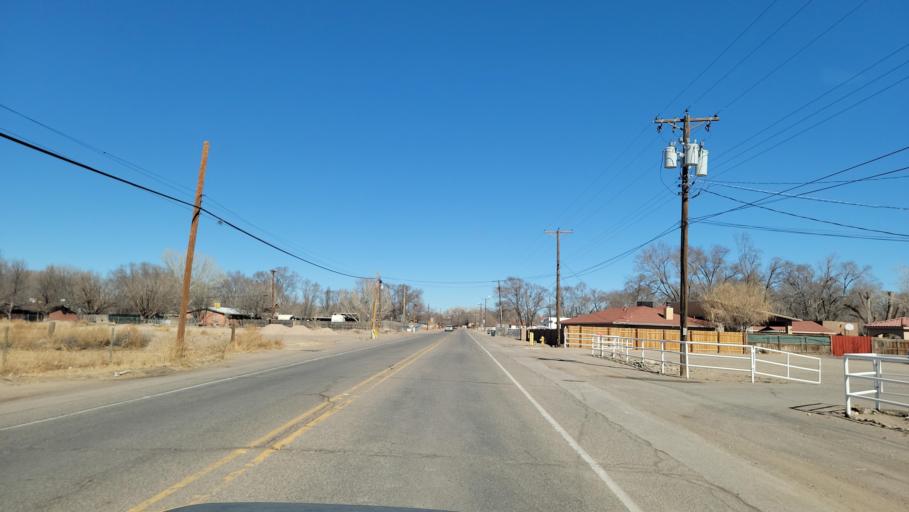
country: US
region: New Mexico
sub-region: Bernalillo County
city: South Valley
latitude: 34.9612
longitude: -106.6958
